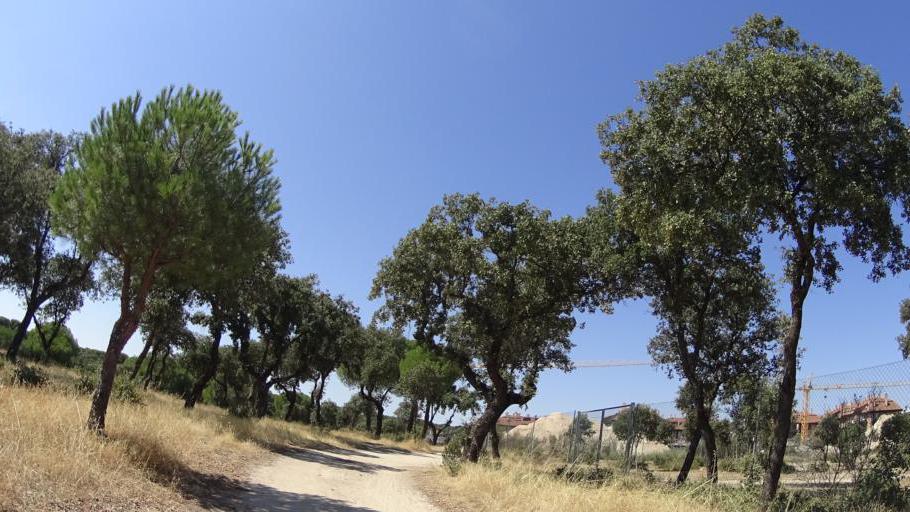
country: ES
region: Madrid
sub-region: Provincia de Madrid
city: Majadahonda
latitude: 40.4407
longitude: -3.8701
